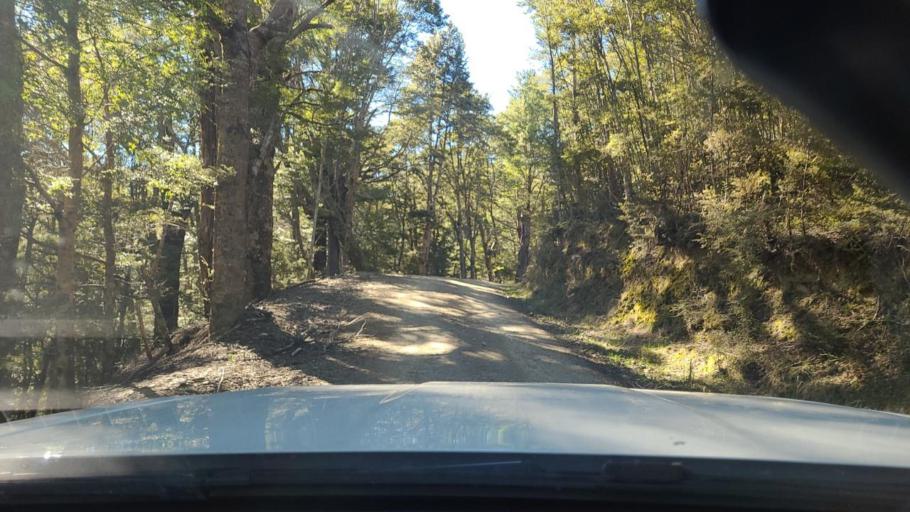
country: NZ
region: Otago
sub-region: Queenstown-Lakes District
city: Kingston
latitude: -45.5386
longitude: 169.0450
